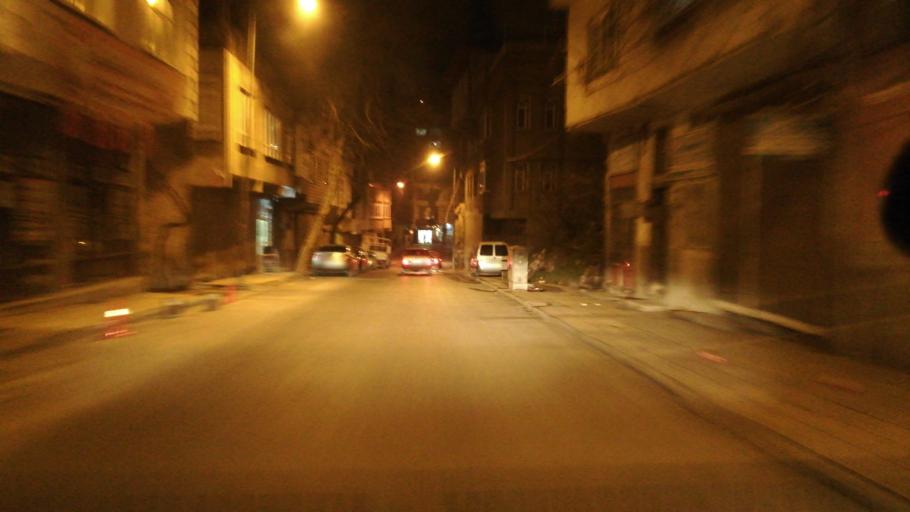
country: TR
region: Kahramanmaras
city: Kahramanmaras
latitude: 37.5855
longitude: 36.9292
